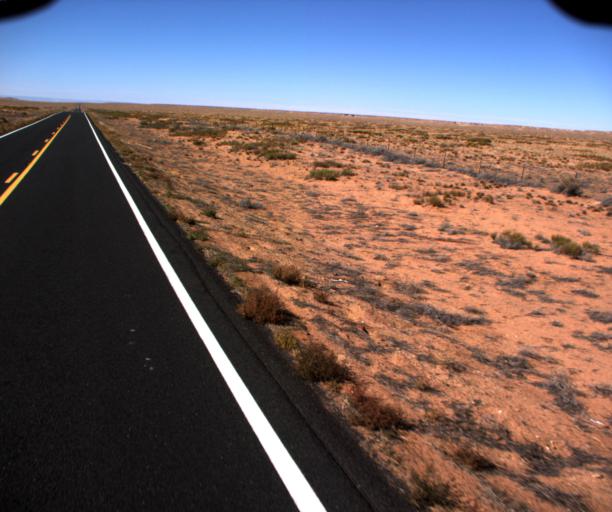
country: US
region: Arizona
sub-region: Coconino County
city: Tuba City
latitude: 36.0216
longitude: -111.1330
